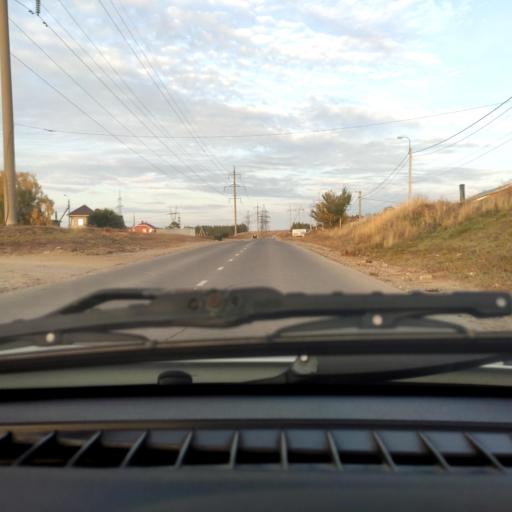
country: RU
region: Samara
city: Zhigulevsk
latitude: 53.4852
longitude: 49.5335
